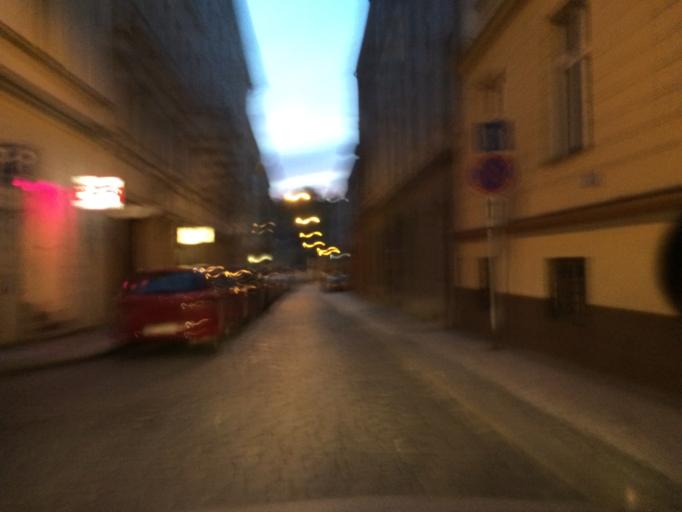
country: CZ
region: Praha
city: Prague
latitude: 50.0832
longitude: 14.4310
